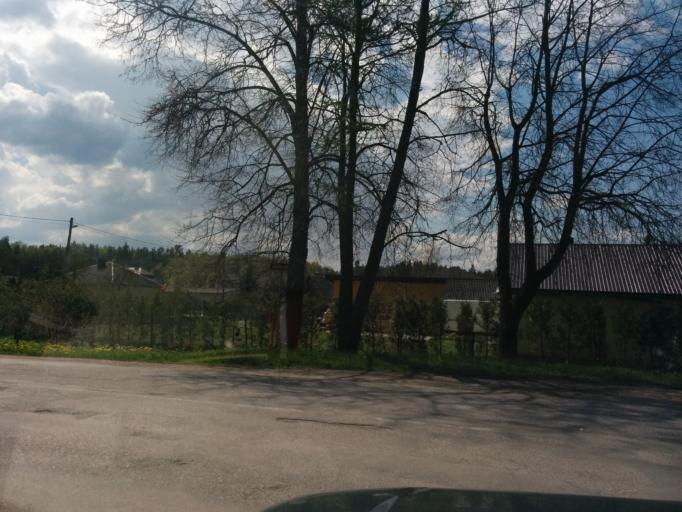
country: LV
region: Jelgava
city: Jelgava
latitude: 56.6213
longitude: 23.7703
